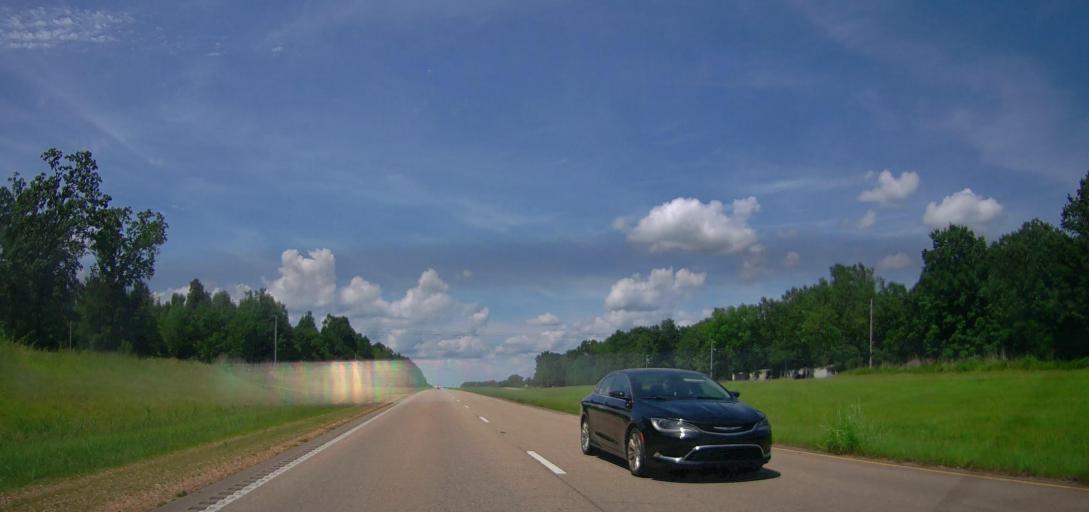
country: US
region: Mississippi
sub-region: Lee County
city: Nettleton
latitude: 34.0119
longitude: -88.6325
